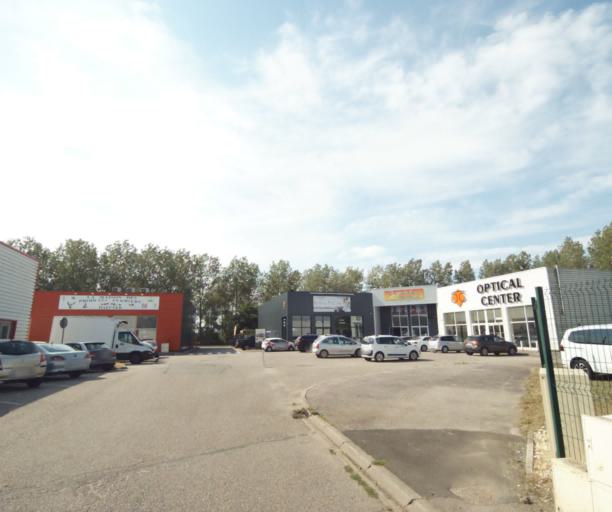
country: FR
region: Lorraine
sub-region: Departement de Meurthe-et-Moselle
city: Chanteheux
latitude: 48.5779
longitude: 6.5169
